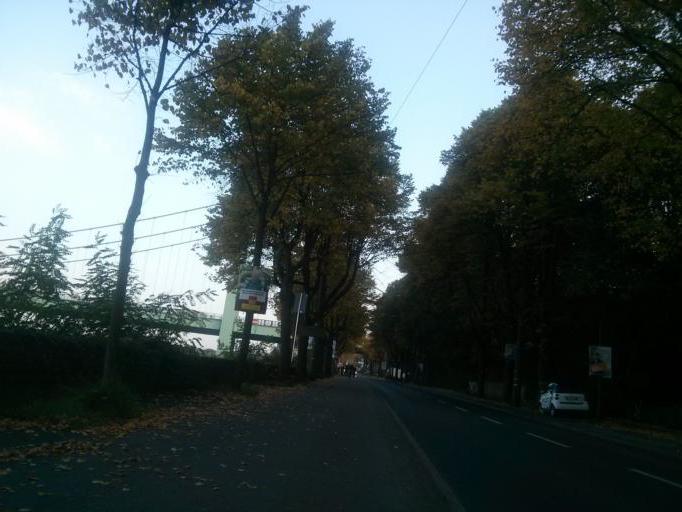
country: DE
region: North Rhine-Westphalia
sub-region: Regierungsbezirk Koln
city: Poll
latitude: 50.8996
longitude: 6.9860
